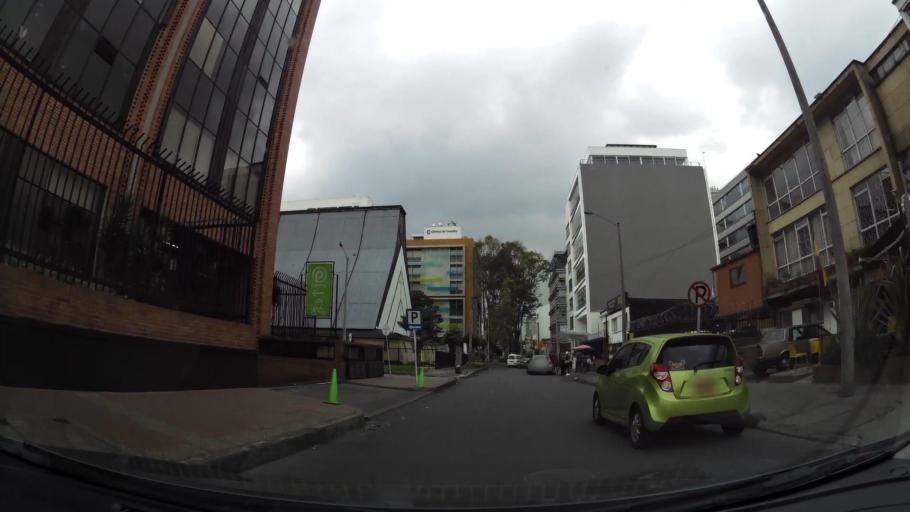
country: CO
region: Bogota D.C.
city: Barrio San Luis
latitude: 4.6700
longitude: -74.0567
